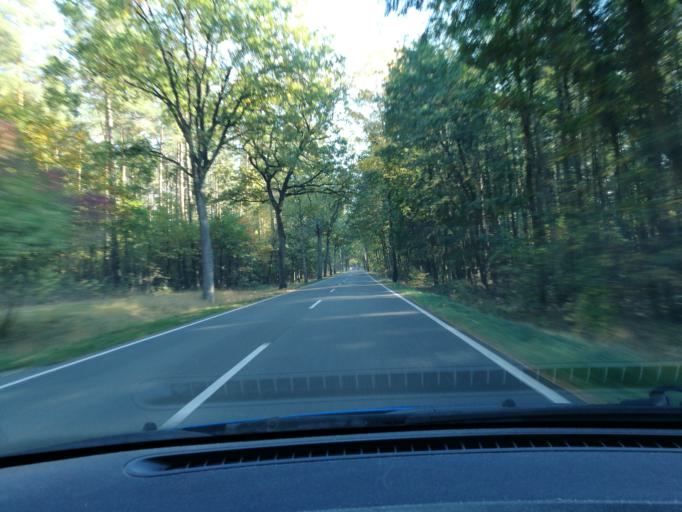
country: DE
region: Lower Saxony
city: Karwitz
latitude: 53.1209
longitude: 10.9862
